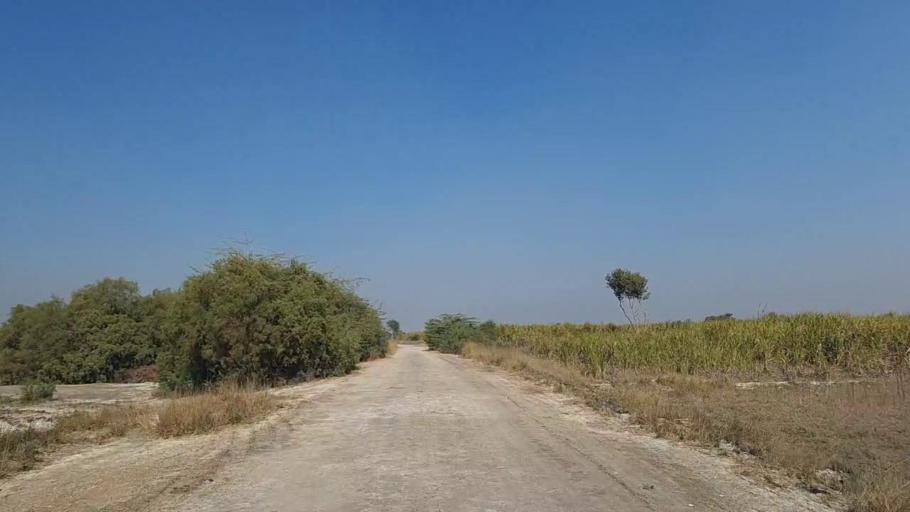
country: PK
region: Sindh
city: Daur
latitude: 26.4927
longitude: 68.3386
